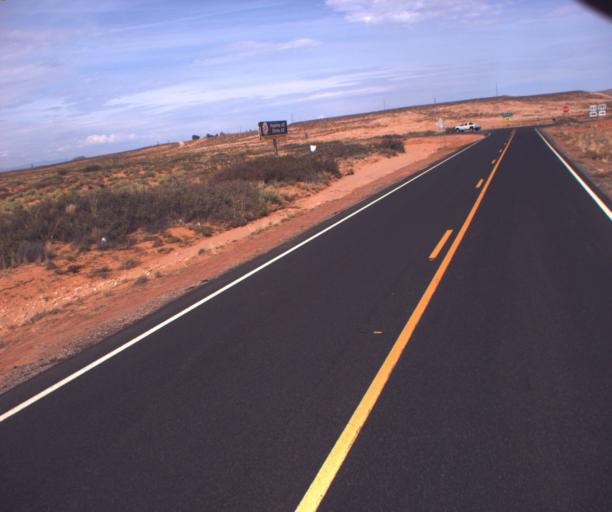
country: US
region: Arizona
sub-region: Apache County
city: Many Farms
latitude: 36.9242
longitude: -109.6156
